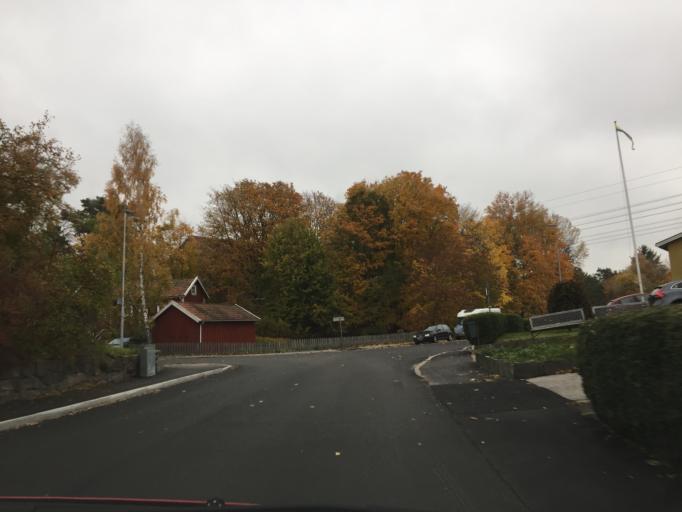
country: SE
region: Vaestra Goetaland
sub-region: Trollhattan
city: Trollhattan
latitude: 58.2720
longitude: 12.2841
